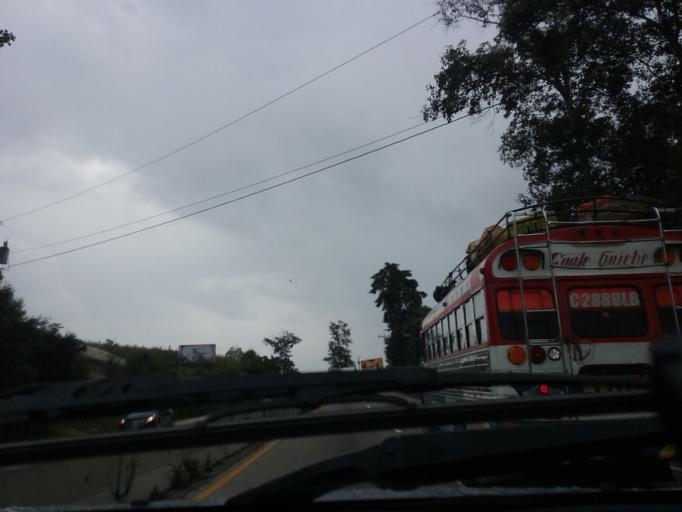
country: GT
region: Chimaltenango
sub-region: Municipio de Zaragoza
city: Zaragoza
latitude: 14.6367
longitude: -90.8982
